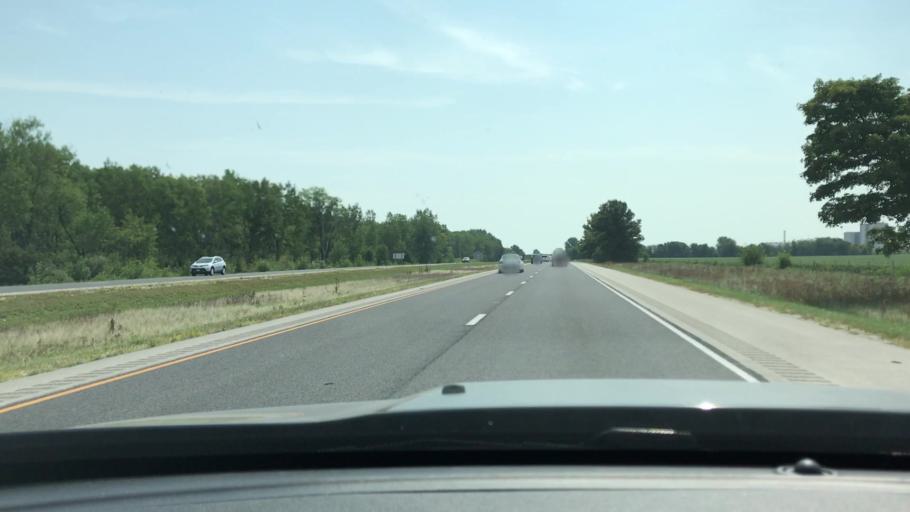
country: US
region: Illinois
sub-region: Henry County
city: Kewanee
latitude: 41.4008
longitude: -89.8891
